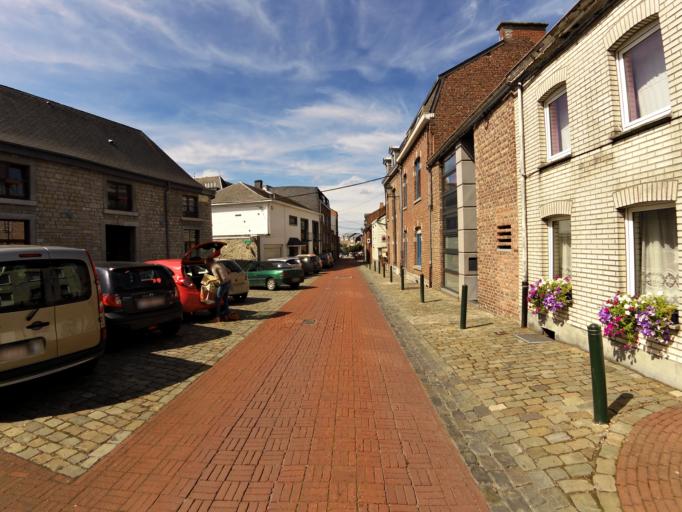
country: BE
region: Wallonia
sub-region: Province du Luxembourg
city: Marche-en-Famenne
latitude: 50.2285
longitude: 5.3453
